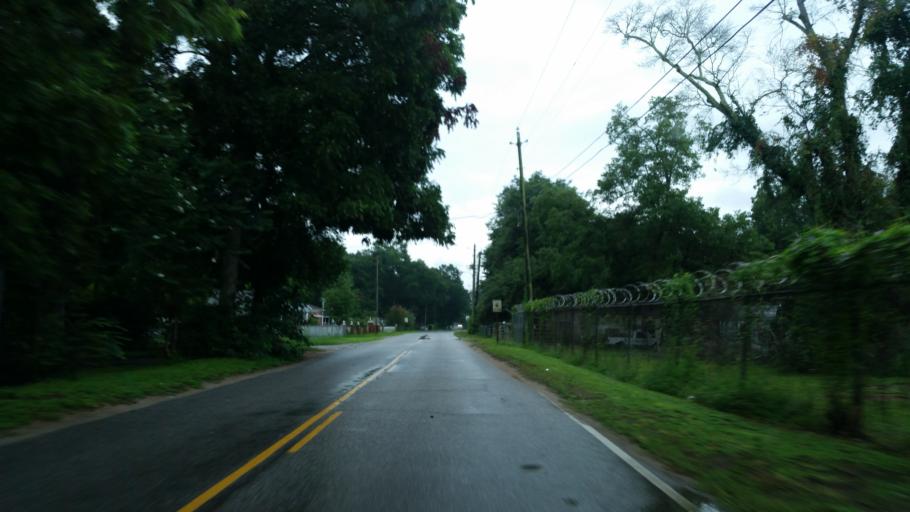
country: US
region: Florida
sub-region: Escambia County
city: West Pensacola
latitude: 30.4292
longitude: -87.2623
